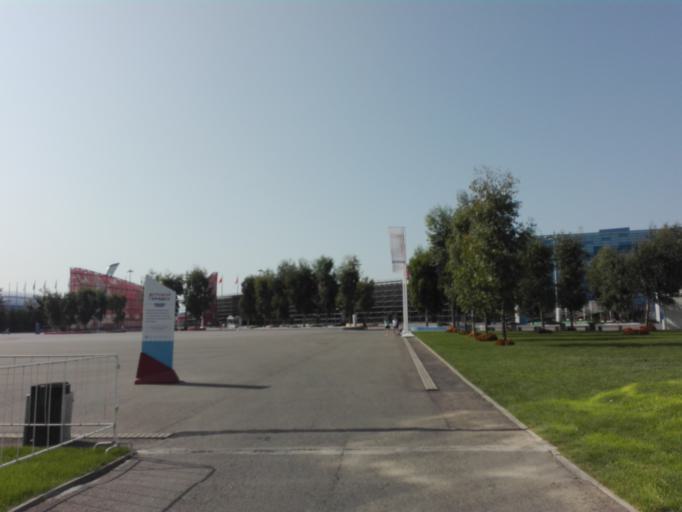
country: RU
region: Krasnodarskiy
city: Adler
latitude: 43.4050
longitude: 39.9606
